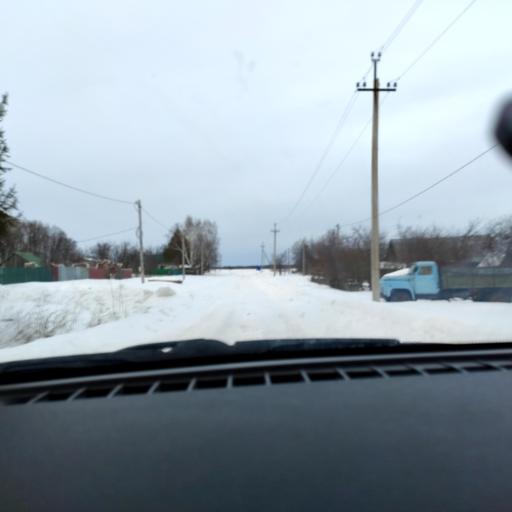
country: RU
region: Bashkortostan
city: Iglino
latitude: 54.7373
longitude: 56.5390
